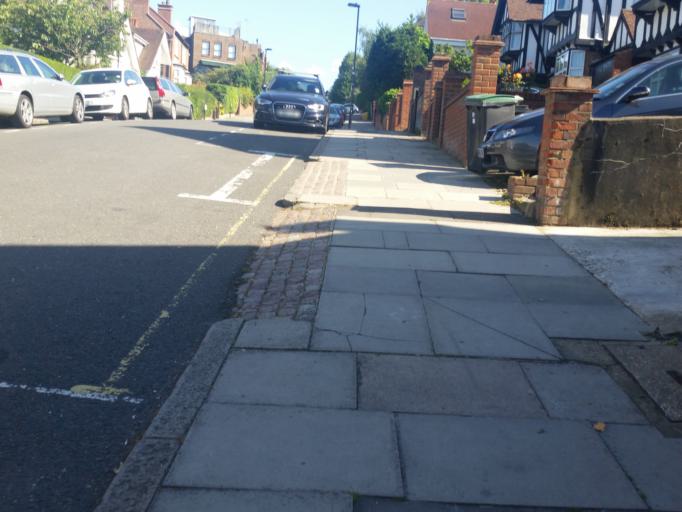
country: GB
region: England
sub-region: Greater London
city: Crouch End
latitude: 51.5809
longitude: -0.1329
